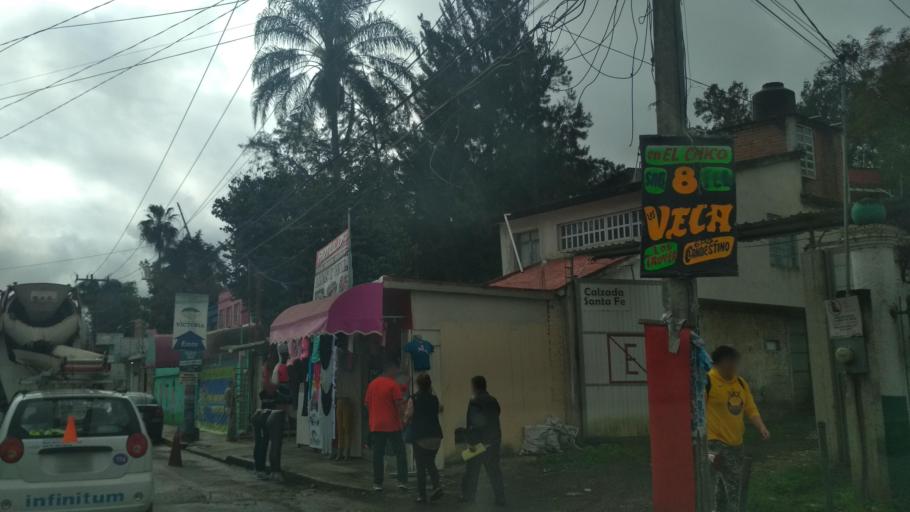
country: MX
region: Veracruz
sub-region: Emiliano Zapata
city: Las Trancas
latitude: 19.5060
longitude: -96.8636
